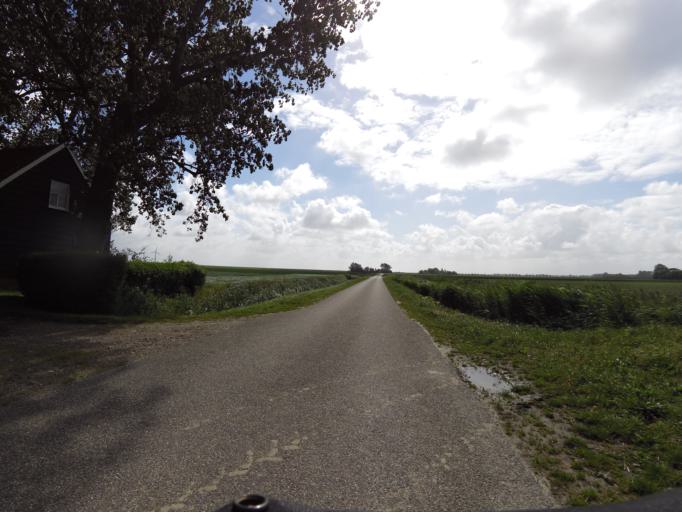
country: NL
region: Zeeland
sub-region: Schouwen-Duiveland
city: Bruinisse
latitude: 51.7008
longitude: 3.9925
